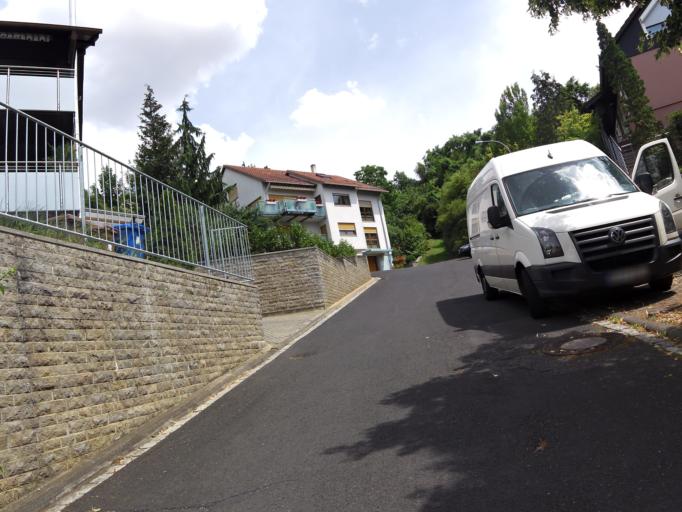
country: DE
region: Bavaria
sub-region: Regierungsbezirk Unterfranken
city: Gerbrunn
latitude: 49.7689
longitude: 9.9949
